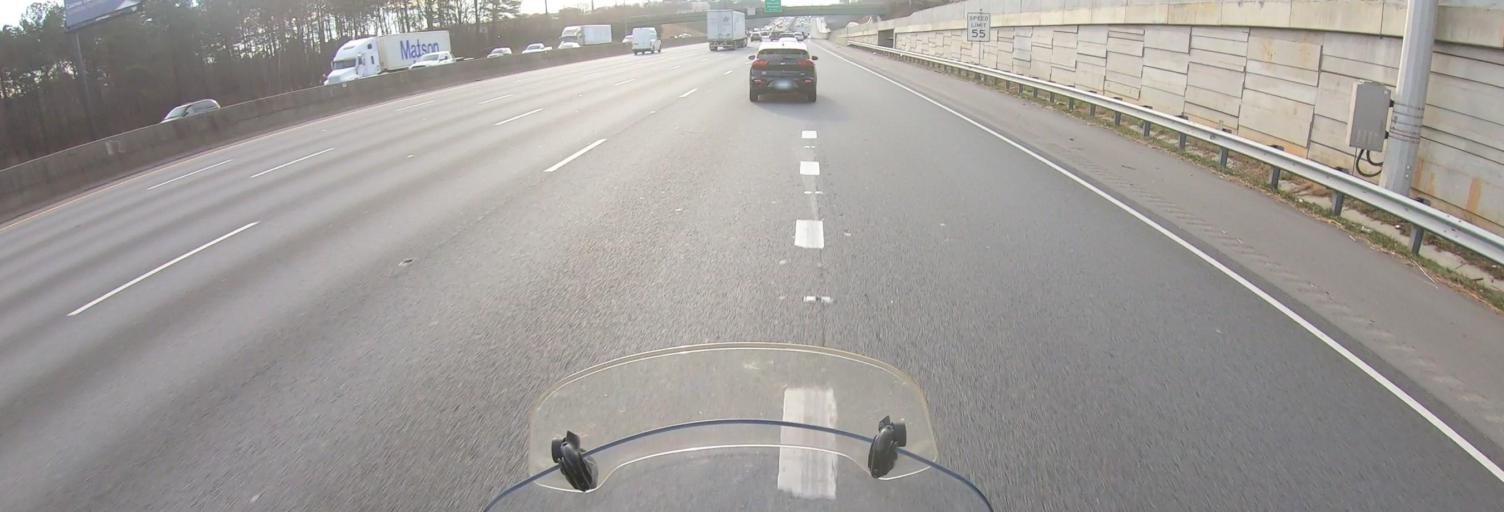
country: US
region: Georgia
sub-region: Cobb County
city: Marietta
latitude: 33.9726
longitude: -84.5334
